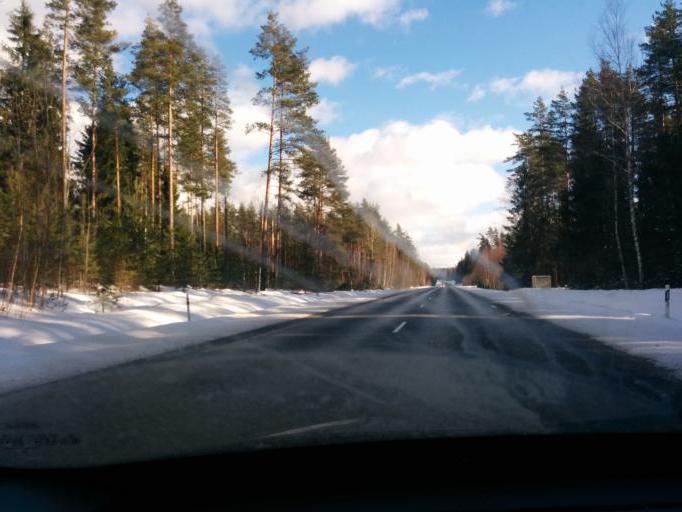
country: LV
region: Jaunpiebalga
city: Jaunpiebalga
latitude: 57.2379
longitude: 26.2956
